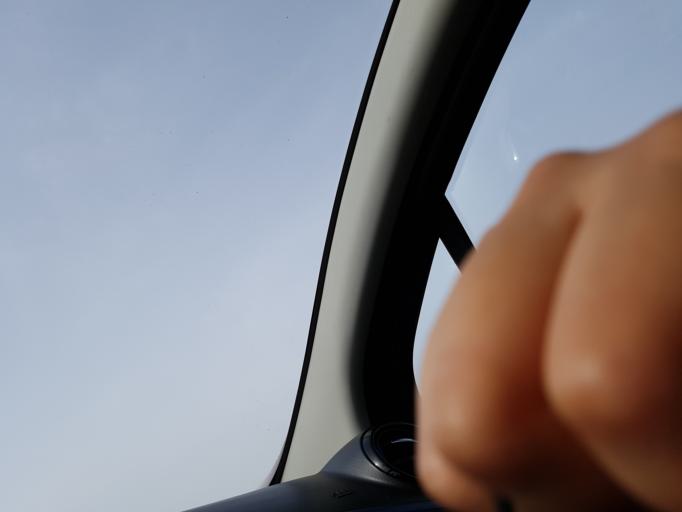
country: OM
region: Al Batinah
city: Al Sohar
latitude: 24.3845
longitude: 56.7012
